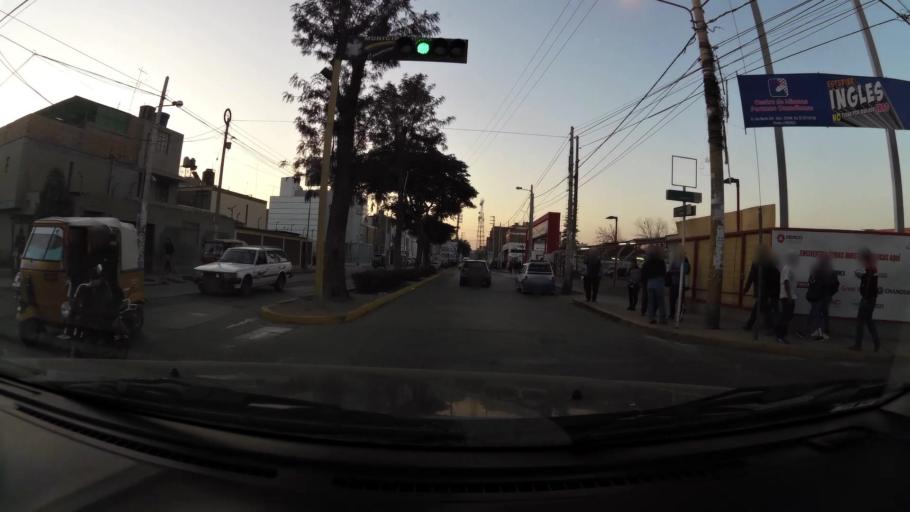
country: PE
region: Ica
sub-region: Provincia de Ica
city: Ica
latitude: -14.0706
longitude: -75.7288
